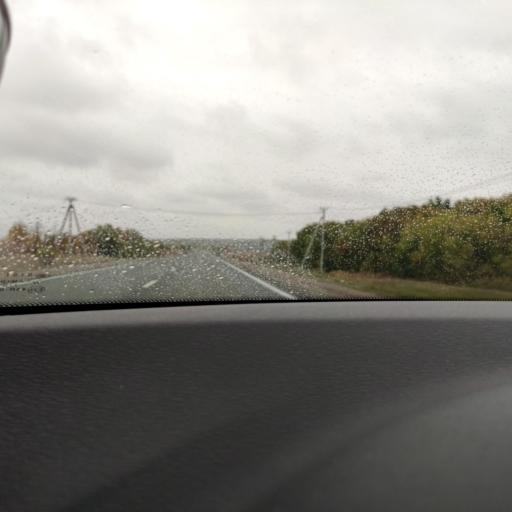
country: RU
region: Samara
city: Mirnyy
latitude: 53.6263
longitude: 50.2487
